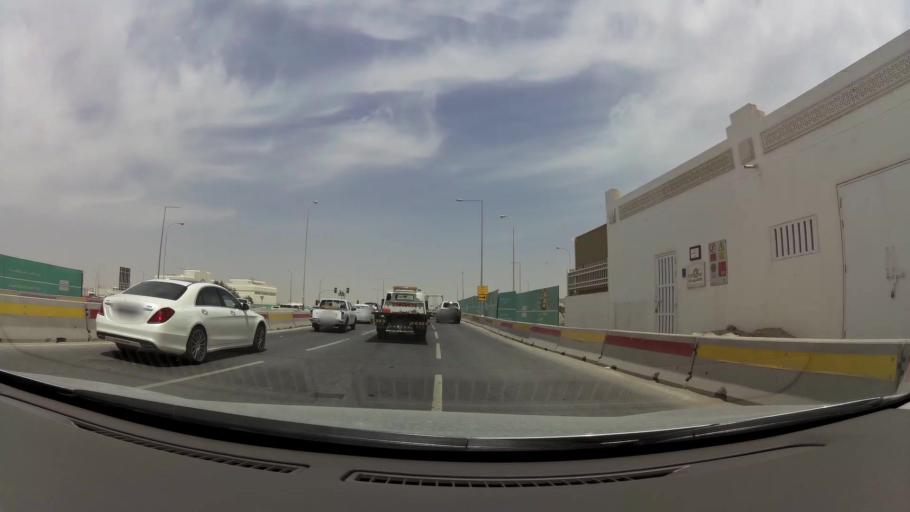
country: QA
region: Baladiyat ar Rayyan
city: Ar Rayyan
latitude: 25.3054
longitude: 51.4122
